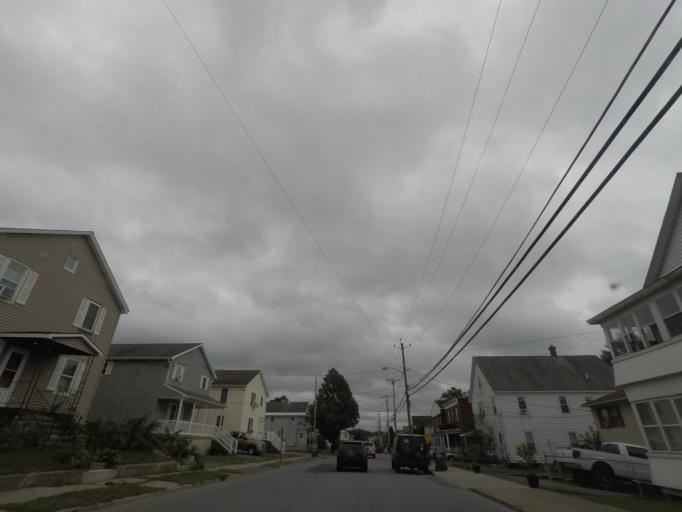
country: US
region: New York
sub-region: Saratoga County
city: Mechanicville
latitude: 42.9113
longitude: -73.6956
